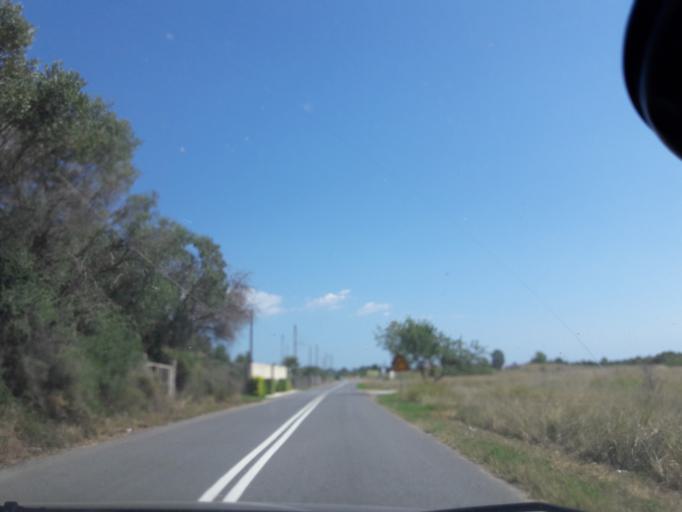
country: GR
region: Central Macedonia
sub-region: Nomos Chalkidikis
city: Nea Kallikrateia
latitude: 40.3335
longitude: 23.0233
